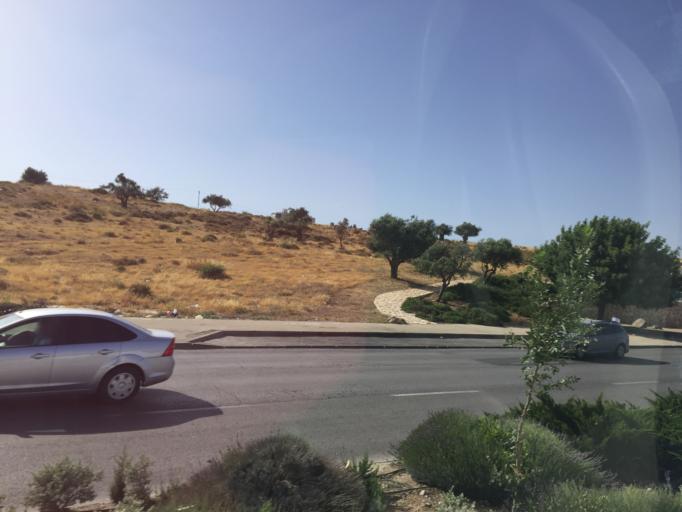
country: PS
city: Khallat Hamamah
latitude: 31.7368
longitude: 35.2109
